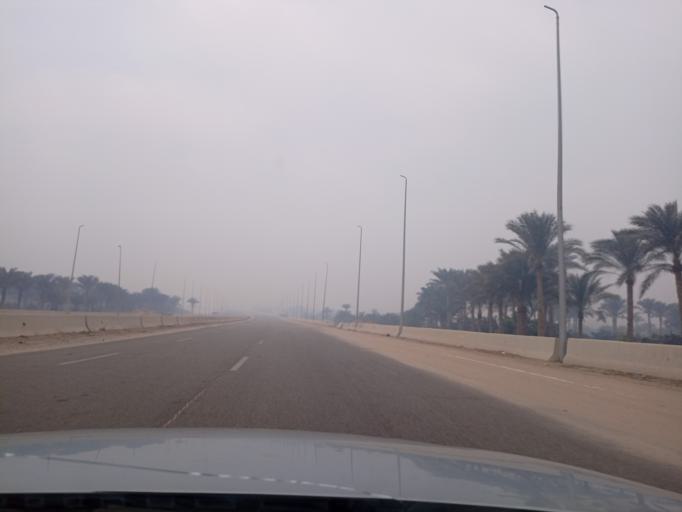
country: EG
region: Al Jizah
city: Al `Ayyat
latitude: 29.6842
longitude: 31.2363
